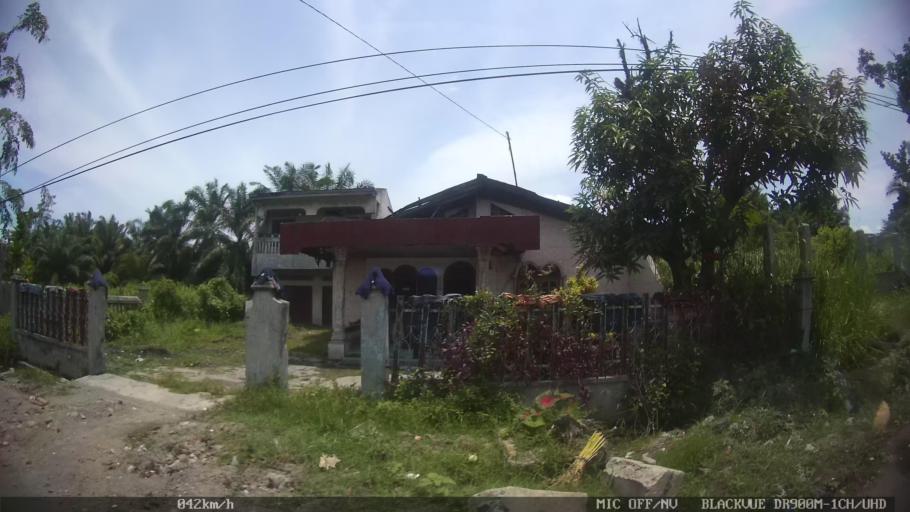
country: ID
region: North Sumatra
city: Labuhan Deli
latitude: 3.7308
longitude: 98.6759
